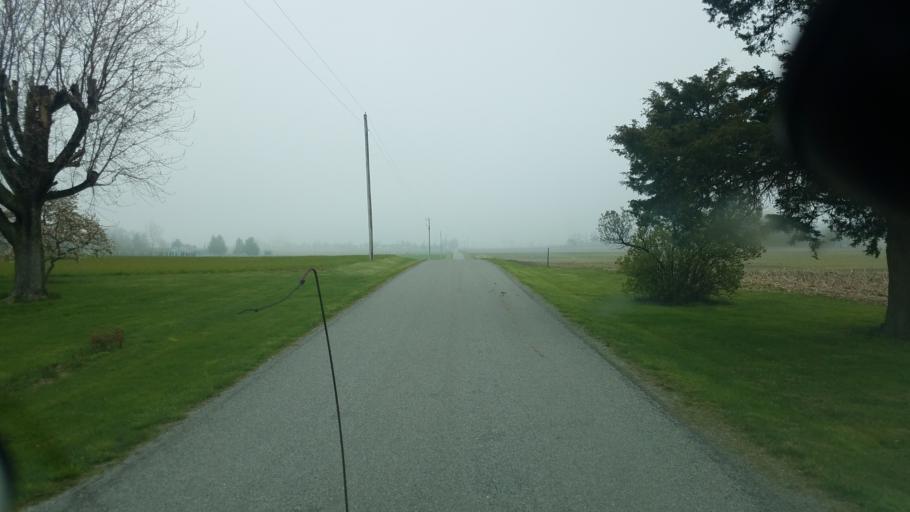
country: US
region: Ohio
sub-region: Logan County
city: Bellefontaine
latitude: 40.3981
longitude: -83.8273
